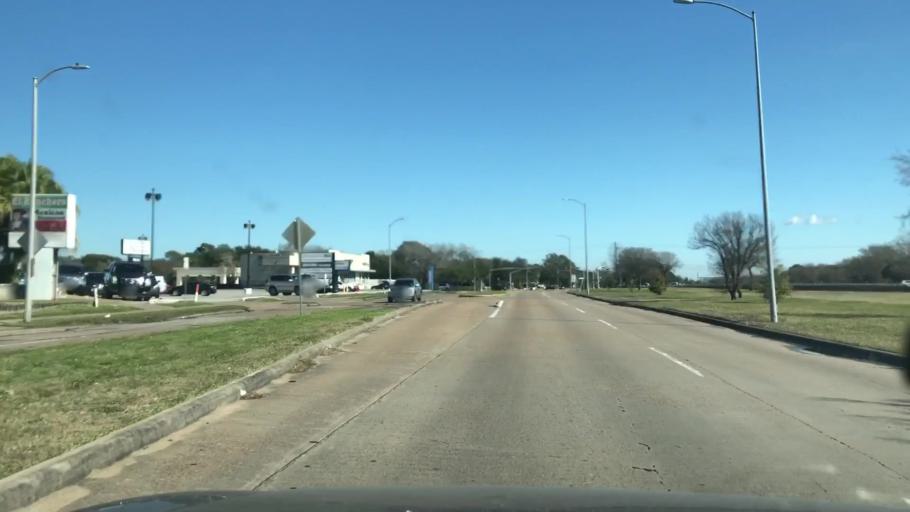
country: US
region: Texas
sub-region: Harris County
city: Bellaire
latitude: 29.6774
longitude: -95.4788
